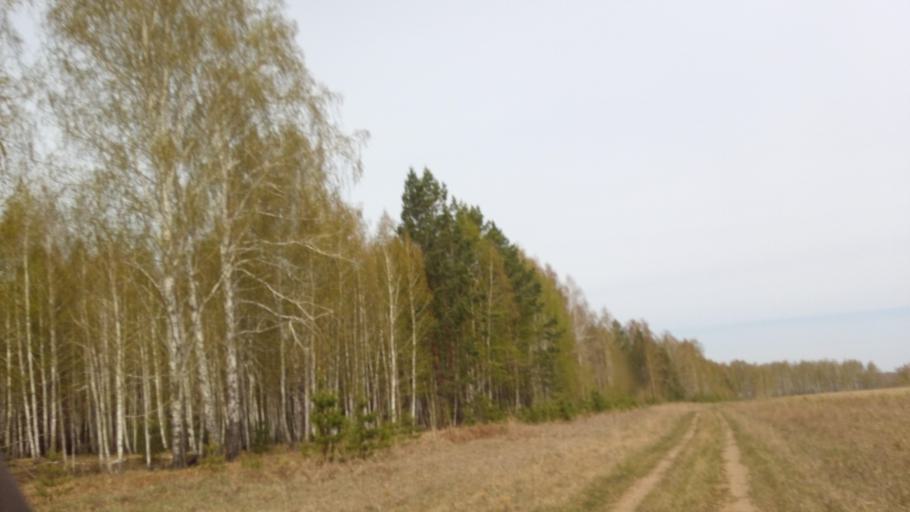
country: RU
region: Chelyabinsk
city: Timiryazevskiy
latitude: 55.0185
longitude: 60.8603
